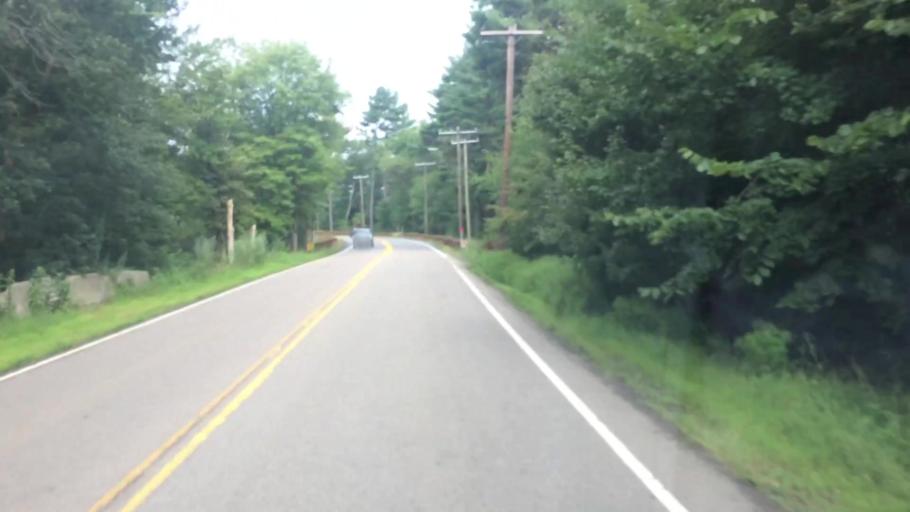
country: US
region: Massachusetts
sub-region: Norfolk County
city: Dedham
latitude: 42.2702
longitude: -71.1885
